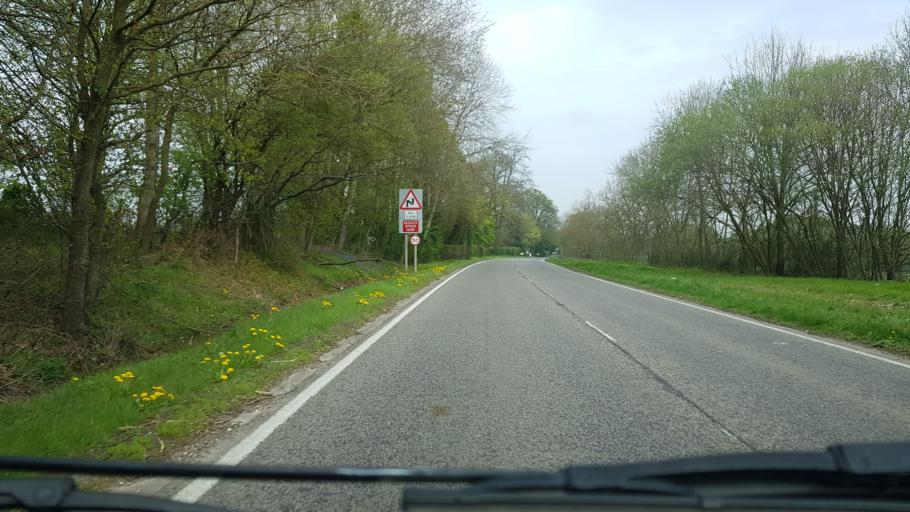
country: GB
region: England
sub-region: Hampshire
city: Kingsclere
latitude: 51.3428
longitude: -1.2588
